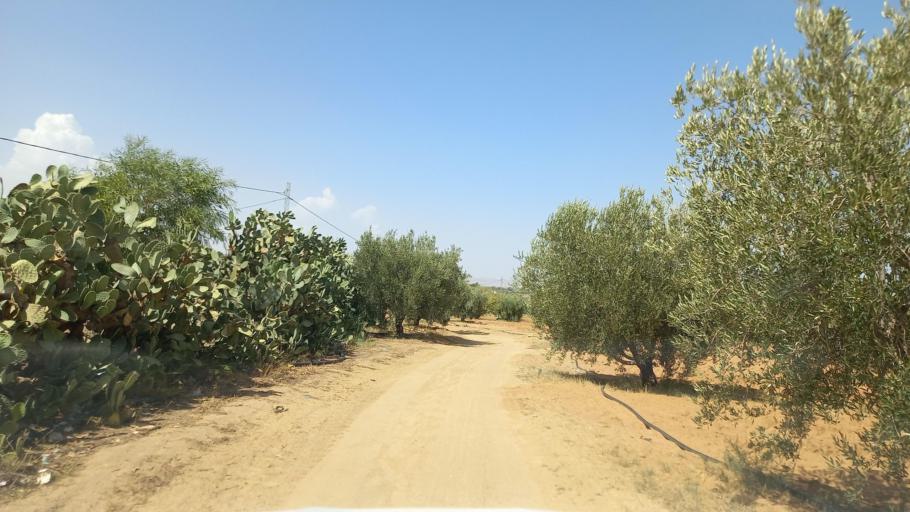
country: TN
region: Al Qasrayn
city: Kasserine
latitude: 35.2201
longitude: 9.0431
